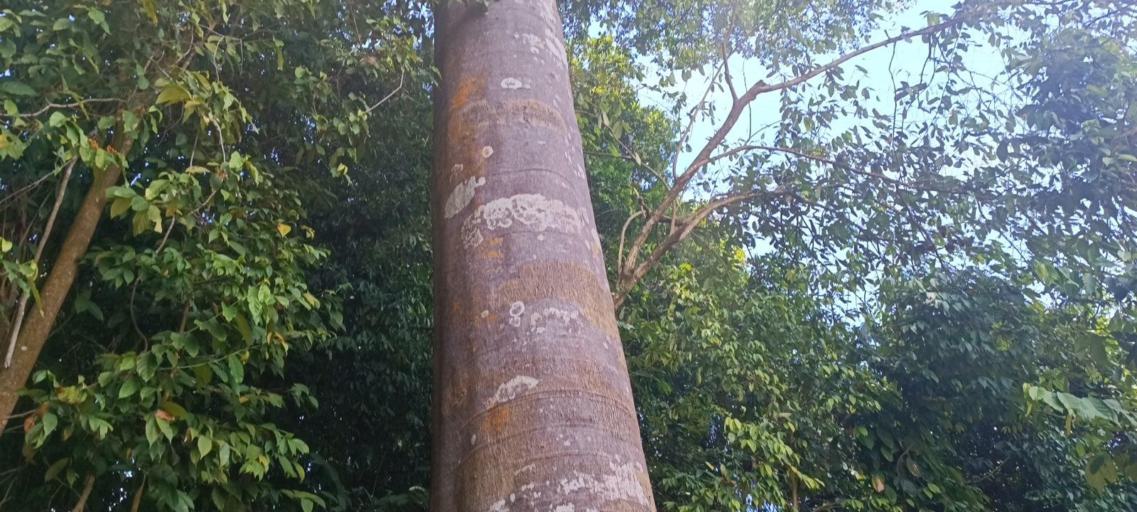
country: MY
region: Penang
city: Juru
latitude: 5.3302
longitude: 100.4115
